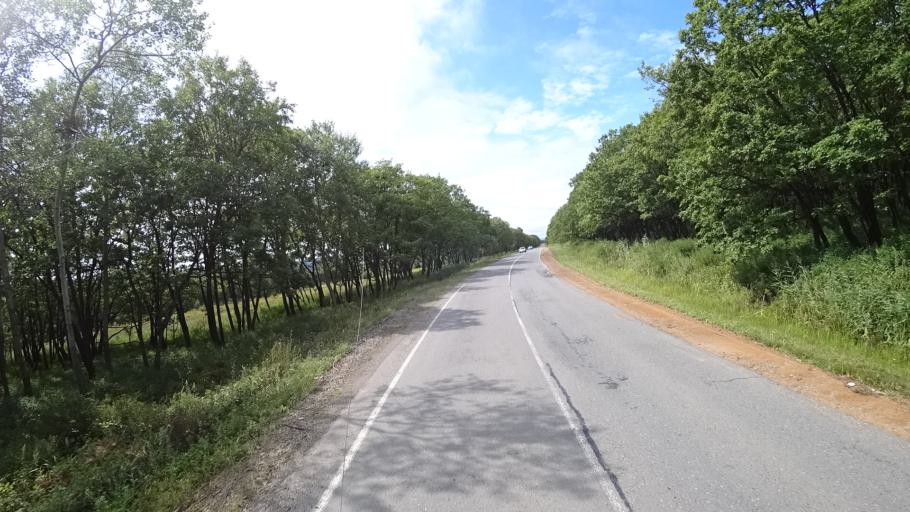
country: RU
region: Primorskiy
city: Lyalichi
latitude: 44.1396
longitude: 132.4128
